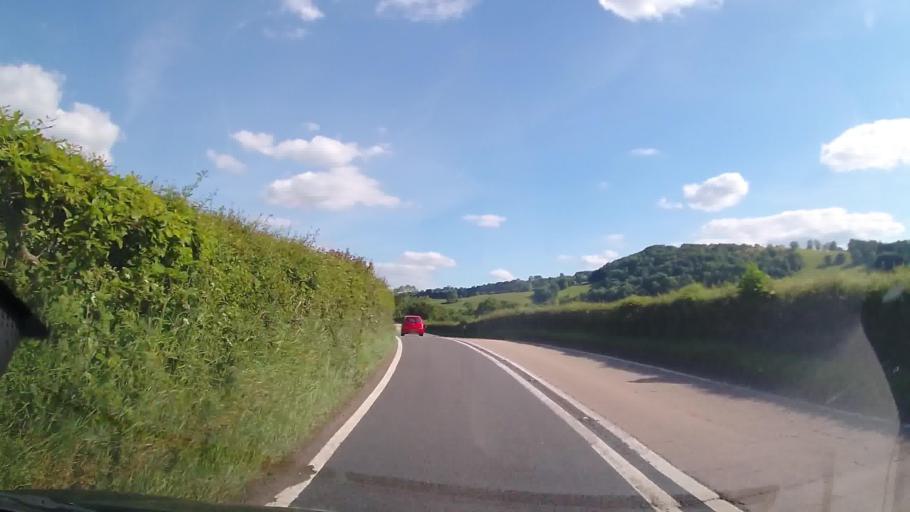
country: GB
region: Wales
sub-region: Sir Powys
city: Welshpool
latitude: 52.6524
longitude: -3.2519
